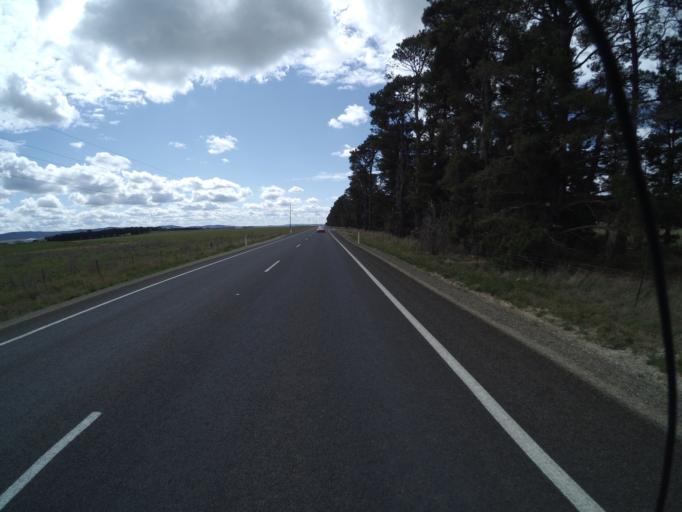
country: AU
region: New South Wales
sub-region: Goulburn Mulwaree
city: Goulburn
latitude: -34.8961
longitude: 149.6855
